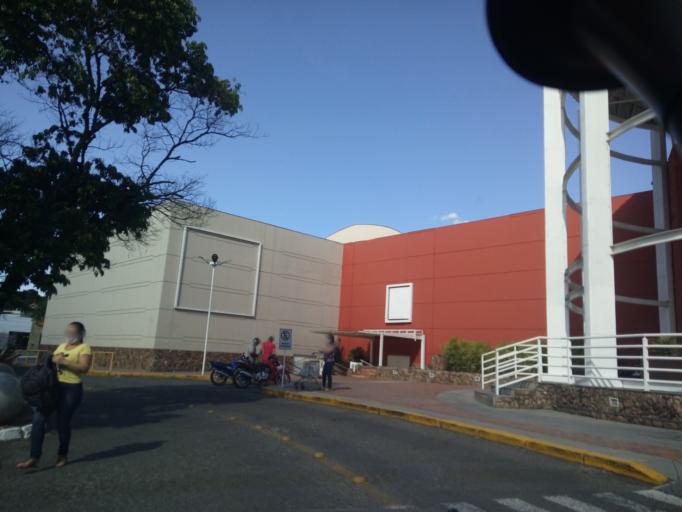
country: BR
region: Rio Grande do Sul
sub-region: Santa Maria
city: Santa Maria
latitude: -29.6972
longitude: -53.7976
